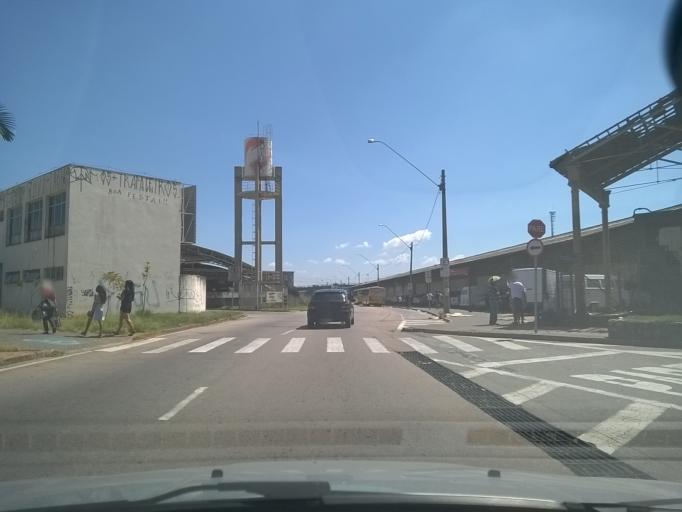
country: BR
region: Sao Paulo
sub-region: Jundiai
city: Jundiai
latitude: -23.1945
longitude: -46.8730
